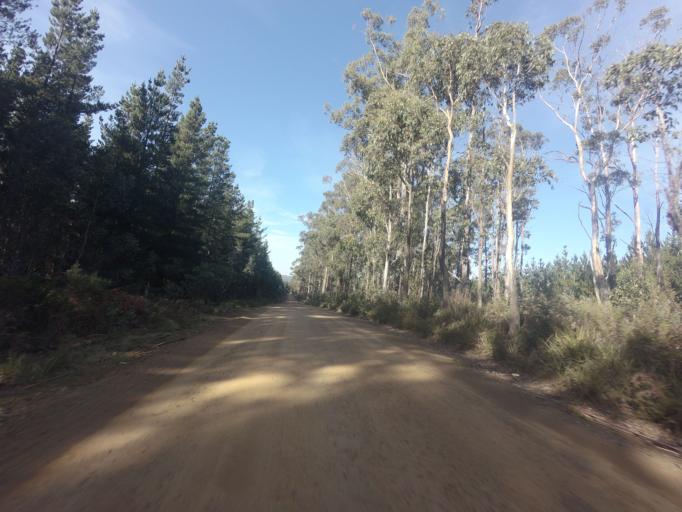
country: AU
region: Tasmania
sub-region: Sorell
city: Sorell
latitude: -42.4875
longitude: 147.4962
